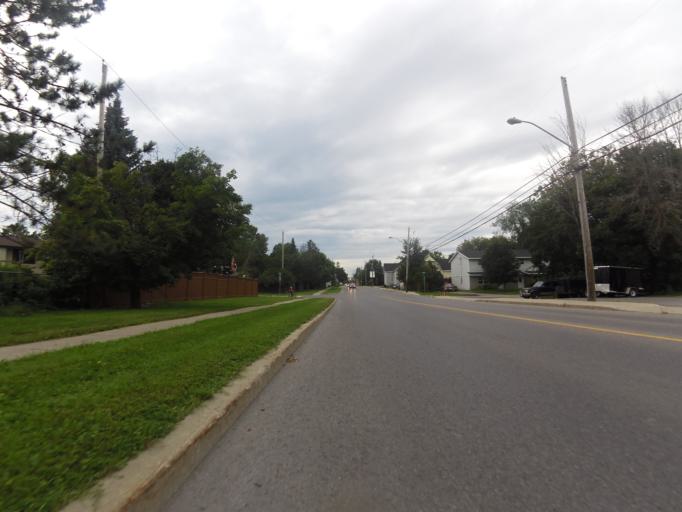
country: CA
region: Ontario
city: Carleton Place
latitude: 45.1332
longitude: -76.1330
